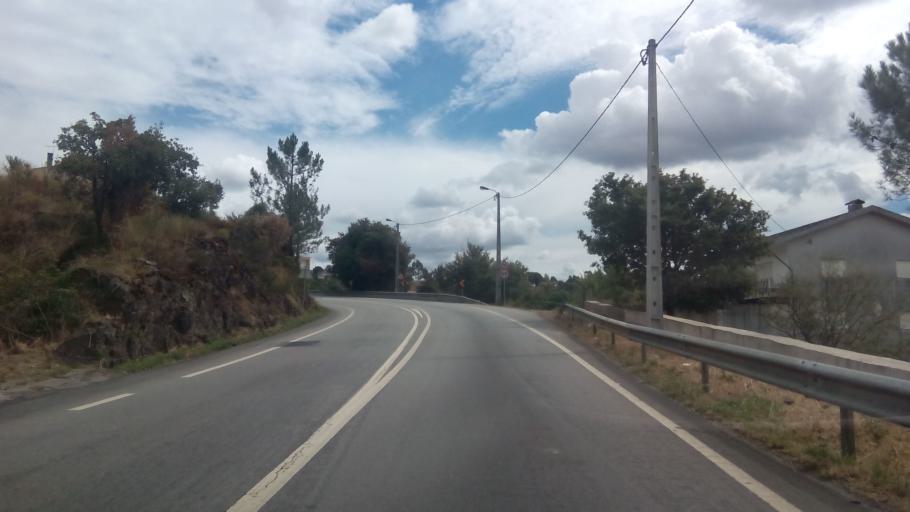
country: PT
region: Porto
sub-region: Paredes
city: Gandra
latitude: 41.1960
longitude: -8.4286
